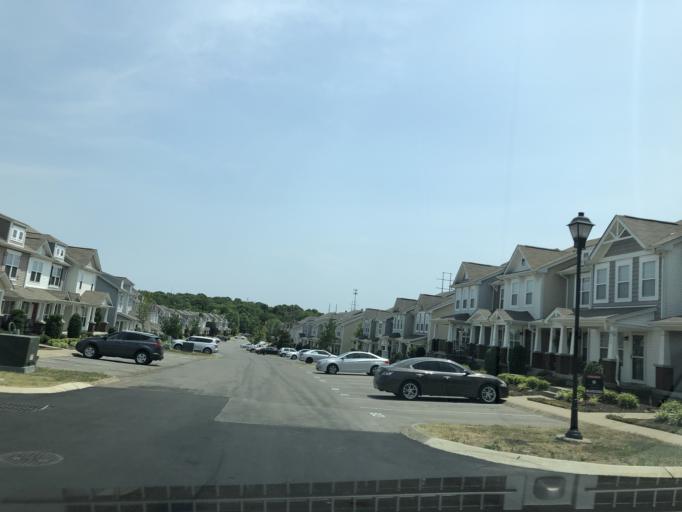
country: US
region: Tennessee
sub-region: Rutherford County
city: La Vergne
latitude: 36.0548
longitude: -86.6140
